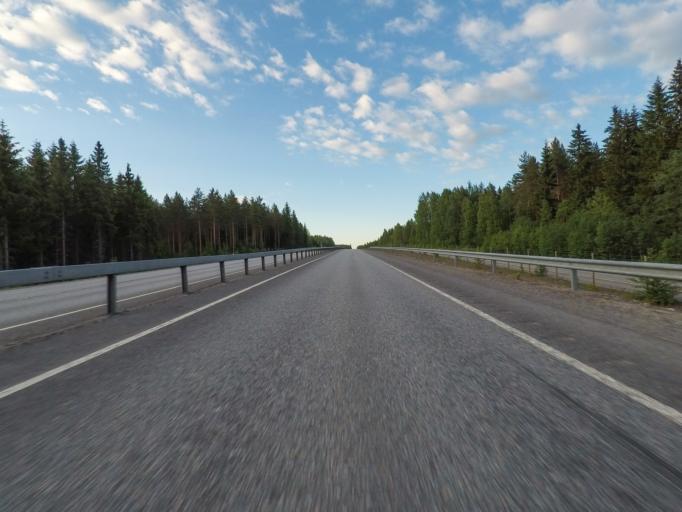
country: FI
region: Southern Savonia
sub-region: Mikkeli
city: Maentyharju
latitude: 61.4900
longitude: 26.7742
